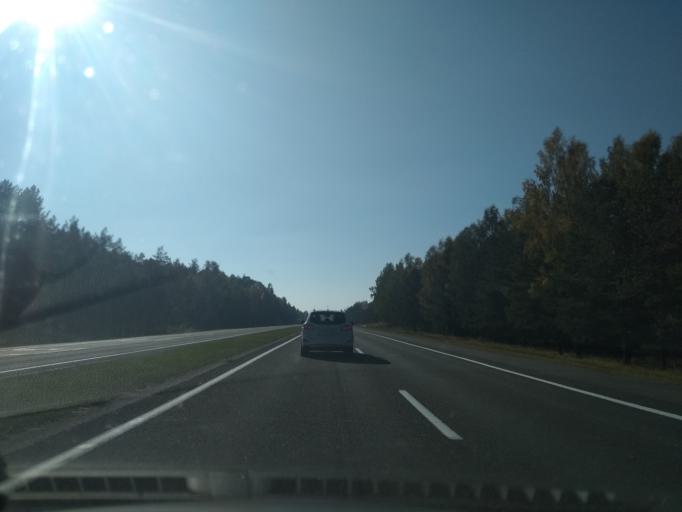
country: BY
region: Brest
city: Ivatsevichy
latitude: 52.8008
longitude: 25.5684
